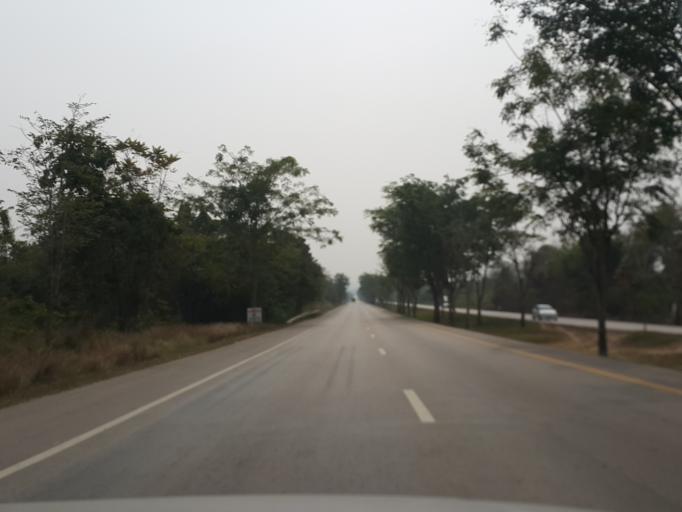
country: TH
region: Lampang
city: Ko Kha
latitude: 18.1243
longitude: 99.3924
